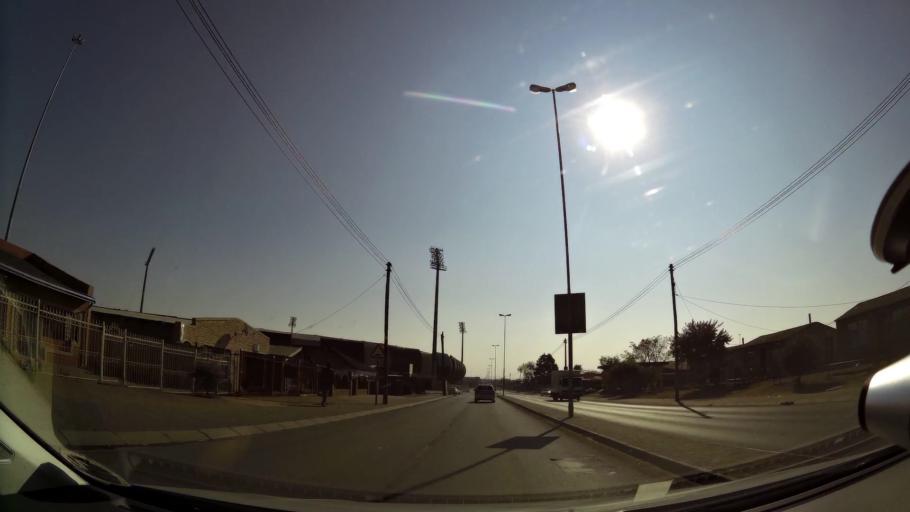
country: ZA
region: Orange Free State
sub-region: Mangaung Metropolitan Municipality
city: Bloemfontein
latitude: -29.1762
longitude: 26.2339
